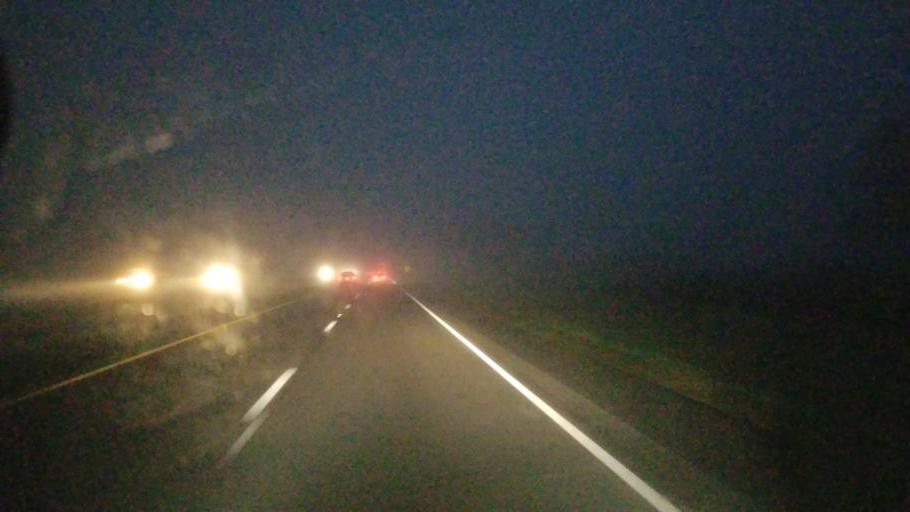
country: US
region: Ohio
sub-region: Ross County
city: Chillicothe
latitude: 39.3639
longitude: -82.9665
